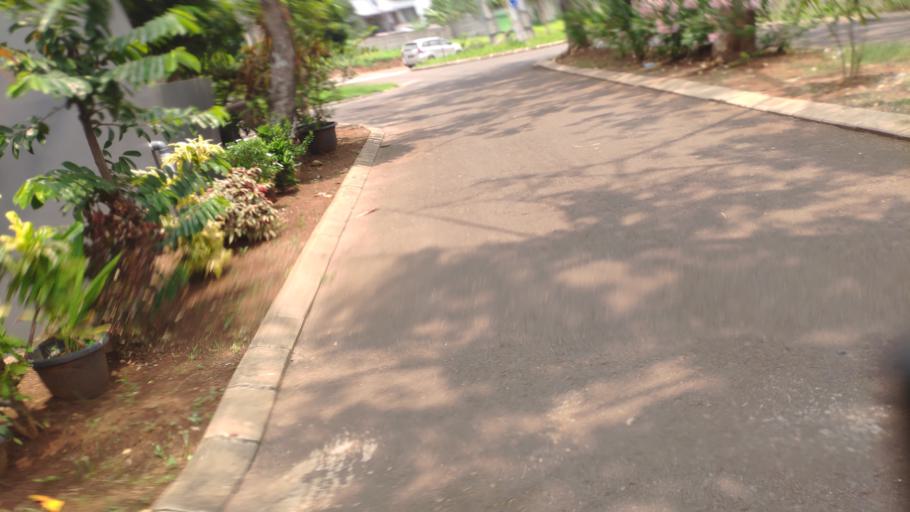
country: ID
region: West Java
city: Sawangan
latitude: -6.3899
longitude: 106.7926
